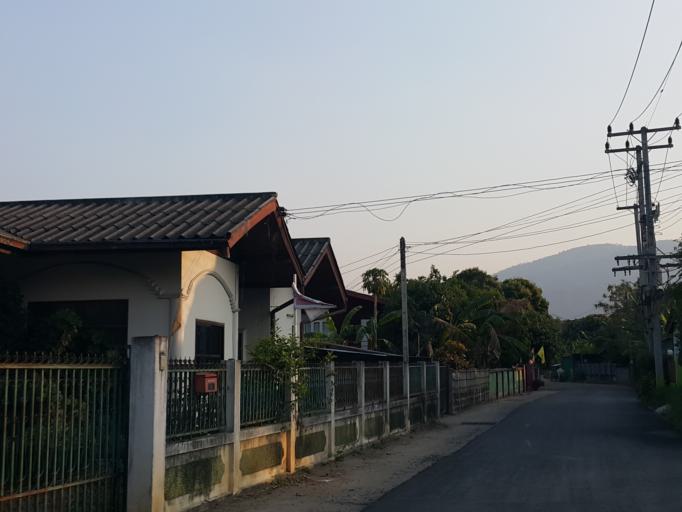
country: TH
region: Chiang Mai
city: San Sai
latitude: 18.9034
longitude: 98.9429
